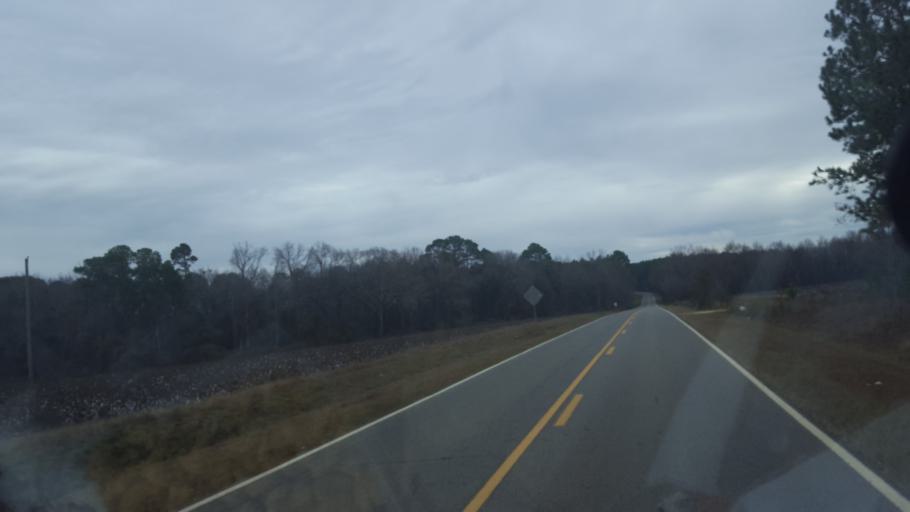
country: US
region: Georgia
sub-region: Wilcox County
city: Rochelle
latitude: 31.7896
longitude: -83.4358
